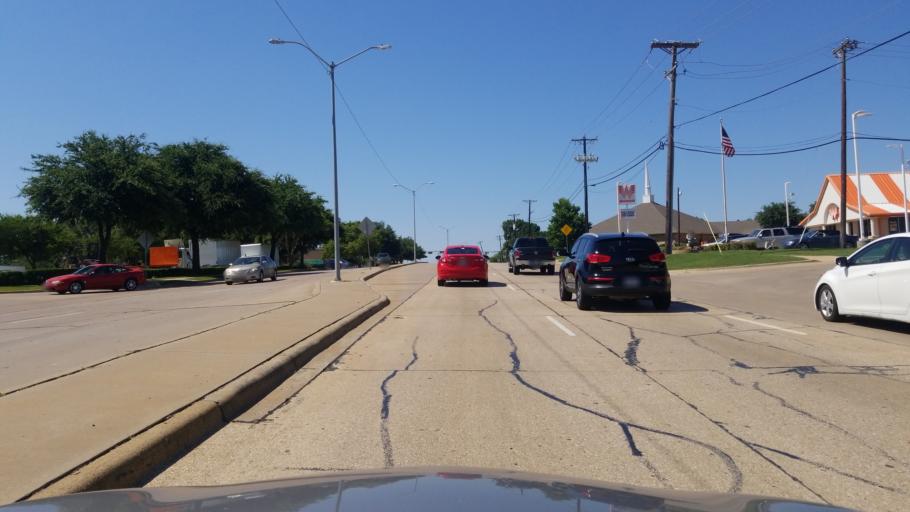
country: US
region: Texas
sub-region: Dallas County
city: Grand Prairie
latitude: 32.6784
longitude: -97.0068
